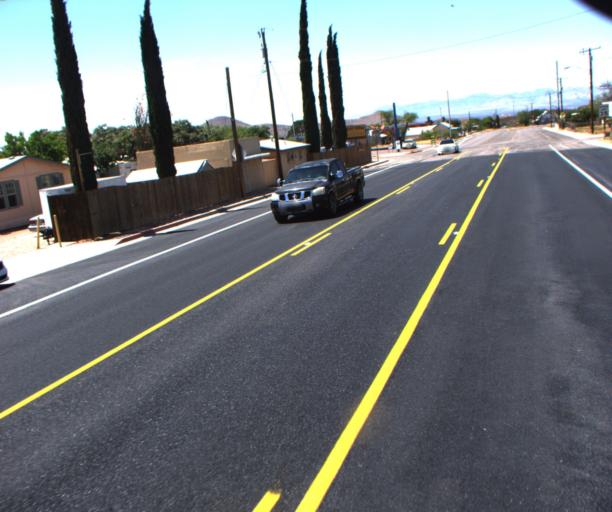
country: US
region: Arizona
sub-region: Cochise County
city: Tombstone
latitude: 31.7143
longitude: -110.0681
